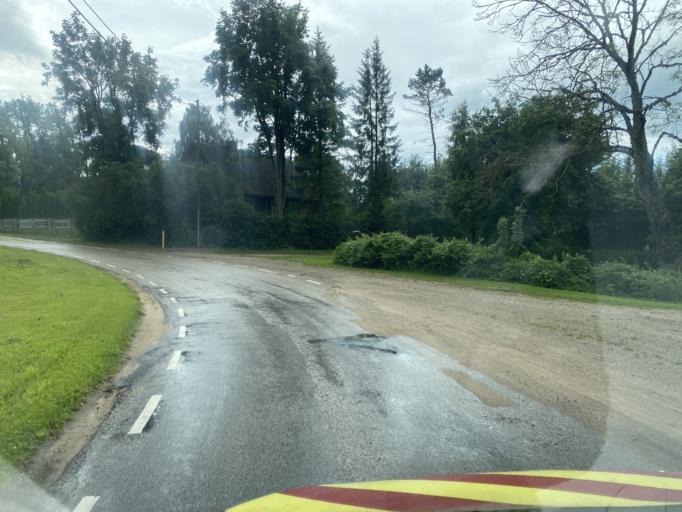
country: EE
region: Valgamaa
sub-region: Torva linn
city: Torva
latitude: 58.0969
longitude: 25.8939
